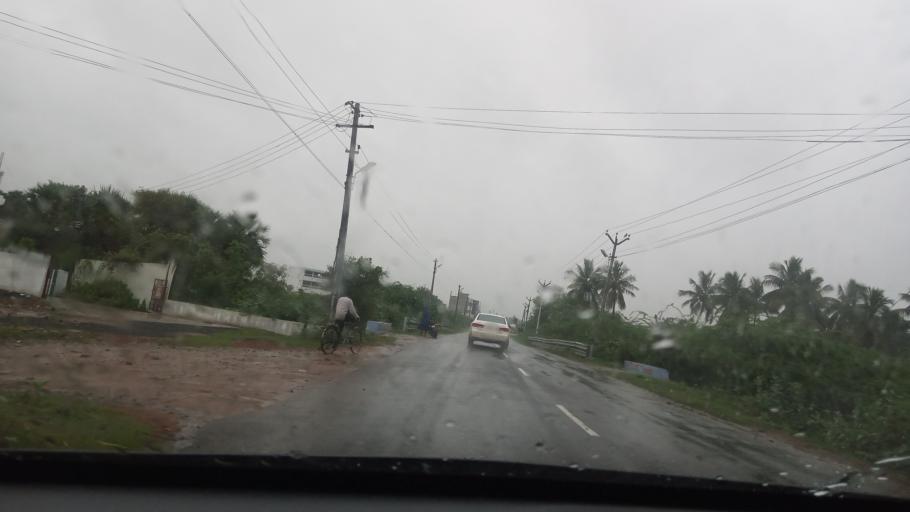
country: IN
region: Tamil Nadu
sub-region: Tiruvannamalai
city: Cheyyar
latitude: 12.6527
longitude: 79.5386
